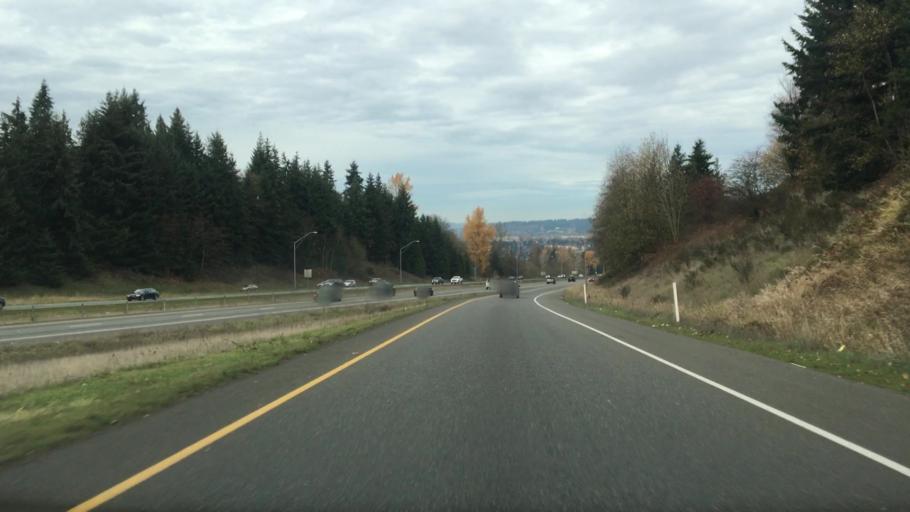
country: US
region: Washington
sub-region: Pierce County
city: Puyallup
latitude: 47.1643
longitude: -122.2961
